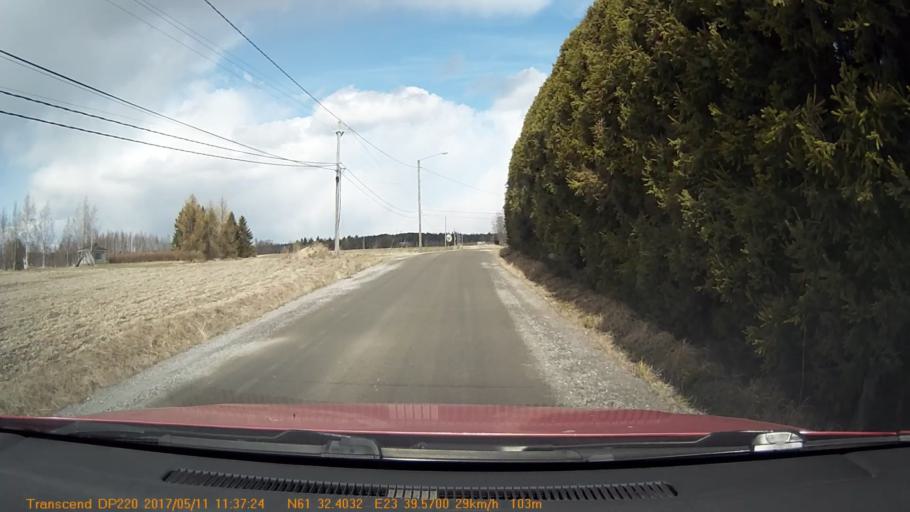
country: FI
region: Pirkanmaa
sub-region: Tampere
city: Yloejaervi
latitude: 61.5399
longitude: 23.6593
